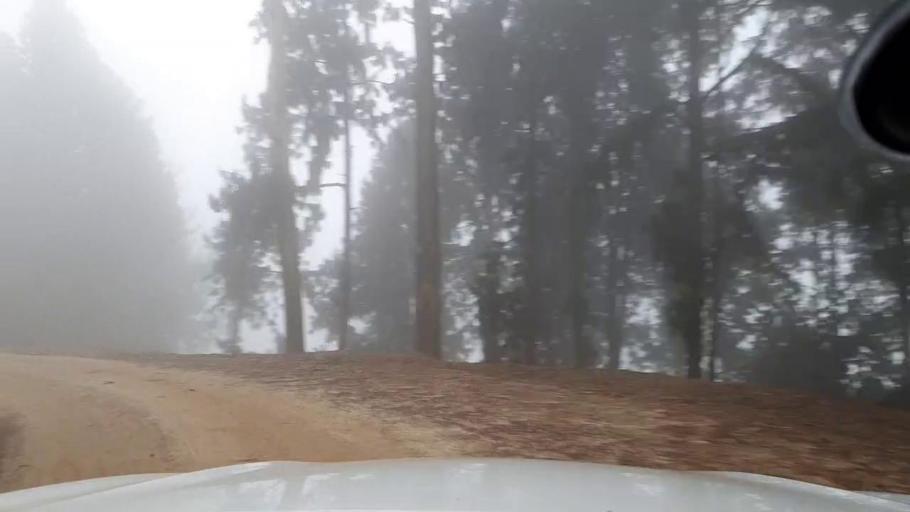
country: BI
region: Cibitoke
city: Cibitoke
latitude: -2.5963
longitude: 29.1941
